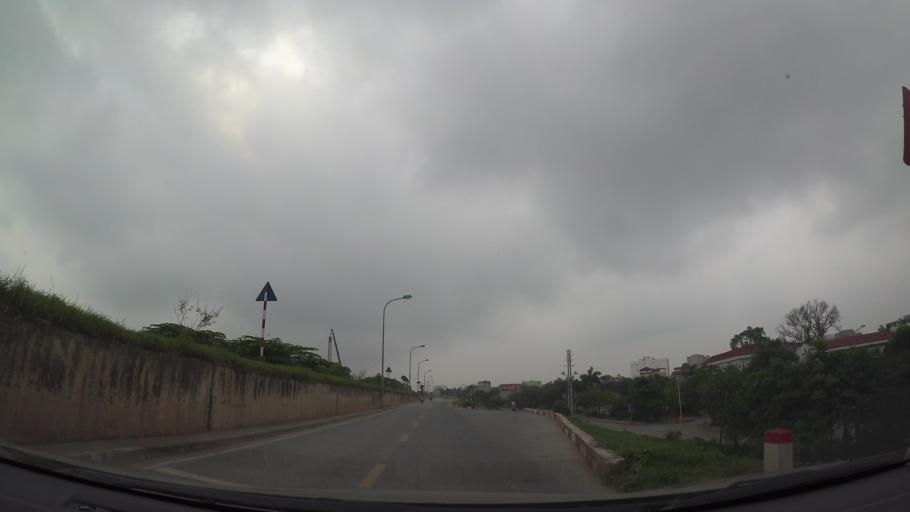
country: VN
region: Ha Noi
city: Trau Quy
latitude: 21.0646
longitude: 105.9190
